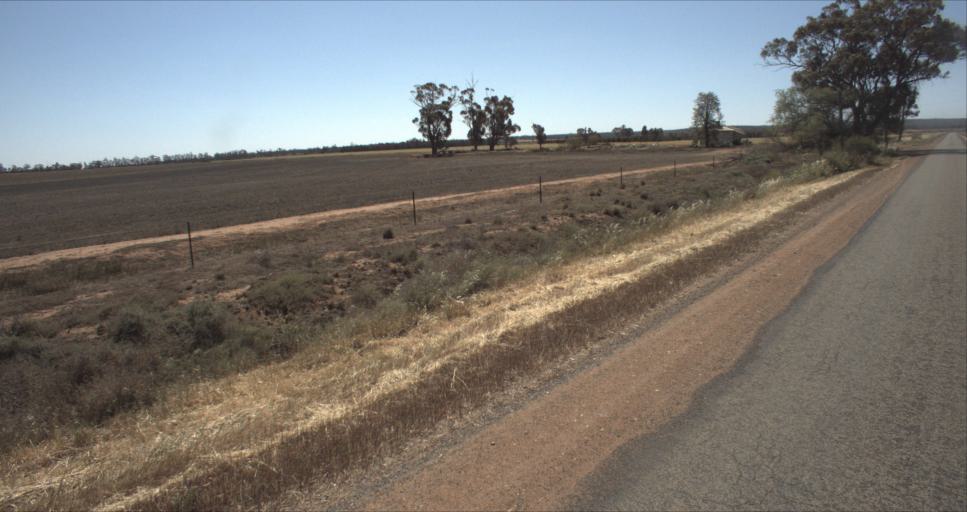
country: AU
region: New South Wales
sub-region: Leeton
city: Leeton
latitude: -34.4746
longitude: 146.4163
